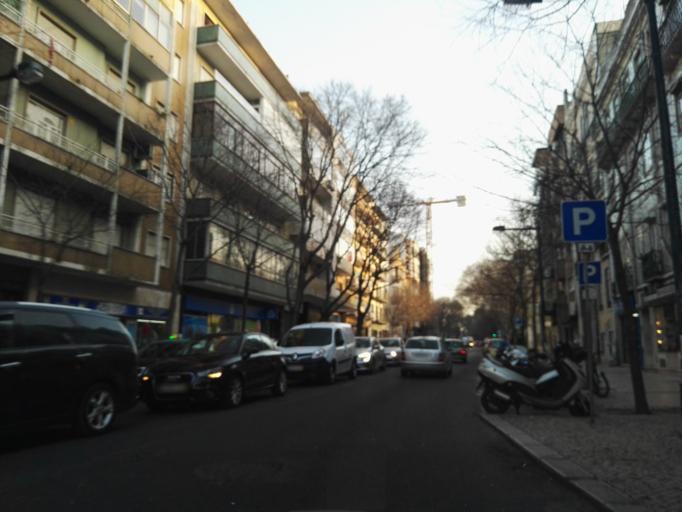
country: PT
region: Lisbon
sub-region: Lisbon
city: Lisbon
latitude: 38.7315
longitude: -9.1408
